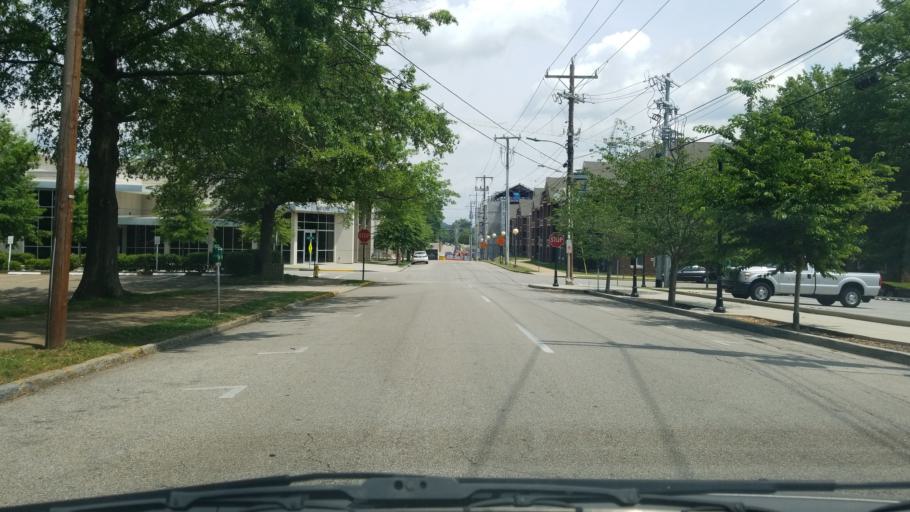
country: US
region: Tennessee
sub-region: Hamilton County
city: Chattanooga
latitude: 35.0474
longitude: -85.3039
